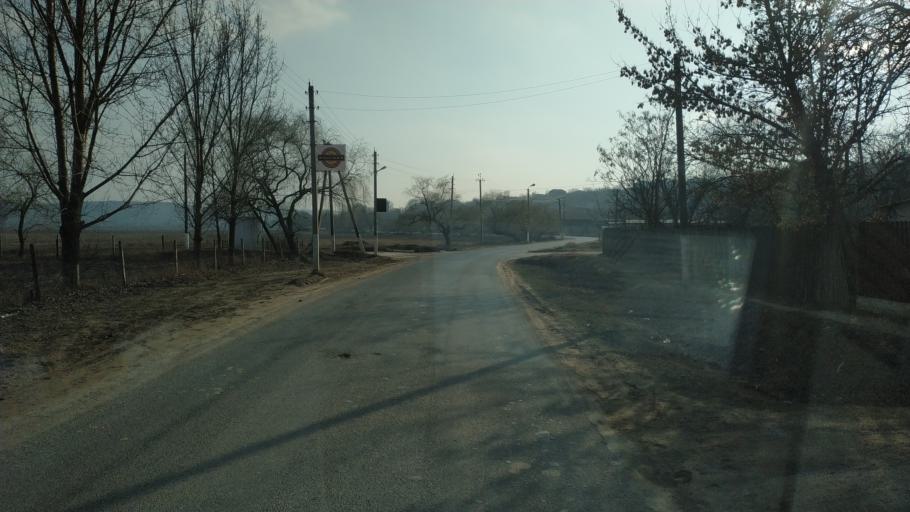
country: MD
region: Hincesti
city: Dancu
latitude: 46.7769
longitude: 28.3474
